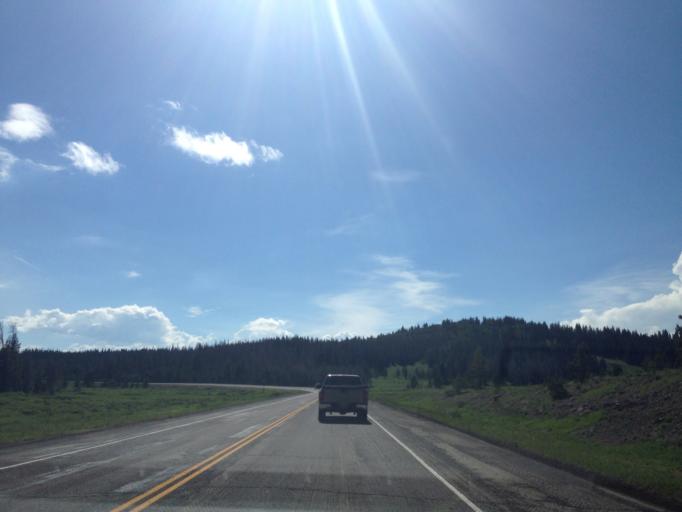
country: US
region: Colorado
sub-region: Routt County
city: Steamboat Springs
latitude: 40.3758
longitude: -106.7305
